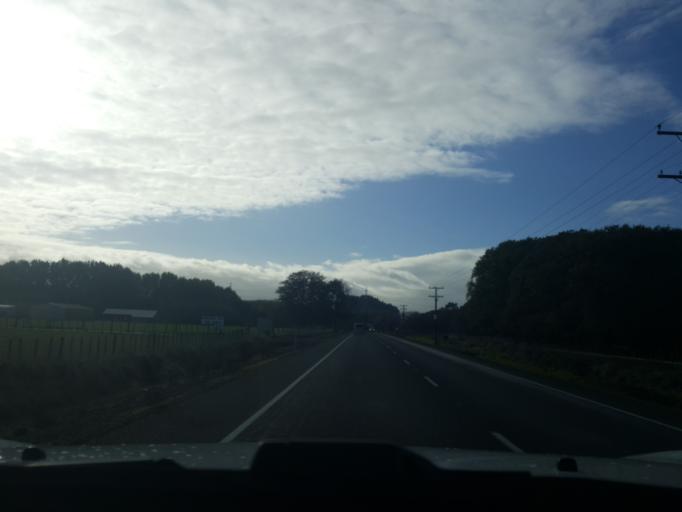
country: NZ
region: Waikato
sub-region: Waipa District
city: Cambridge
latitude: -37.6667
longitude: 175.4928
